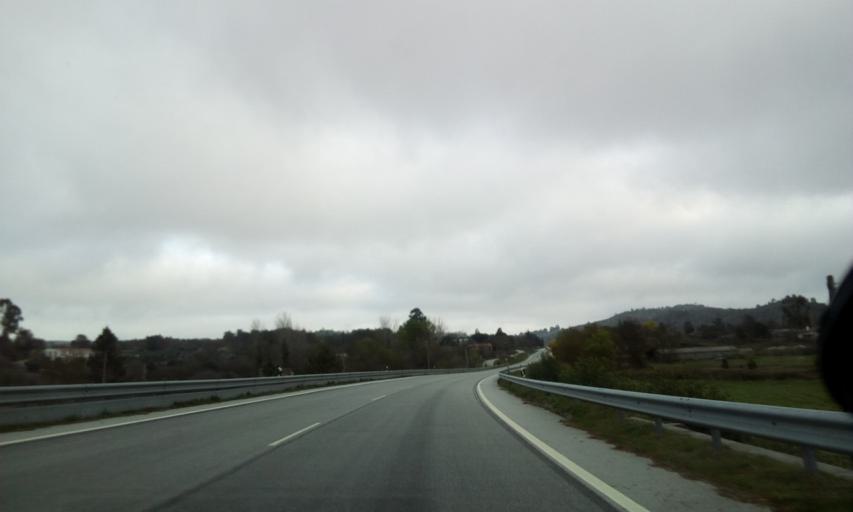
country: PT
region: Guarda
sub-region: Fornos de Algodres
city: Fornos de Algodres
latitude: 40.6336
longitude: -7.5004
